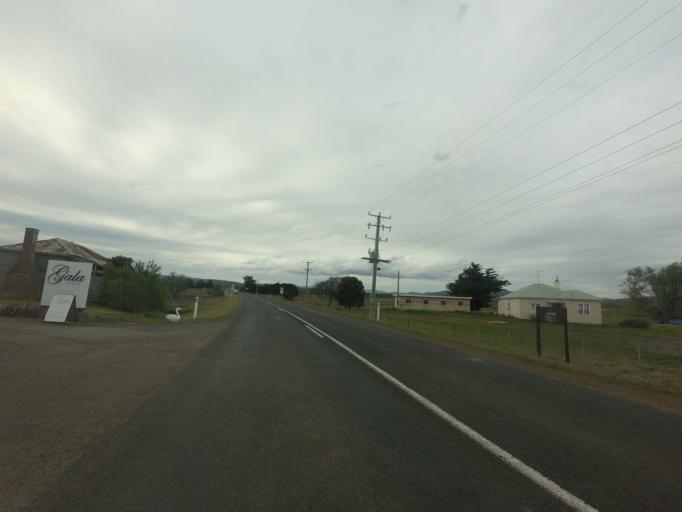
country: AU
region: Tasmania
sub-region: Break O'Day
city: St Helens
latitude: -42.0056
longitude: 148.0688
